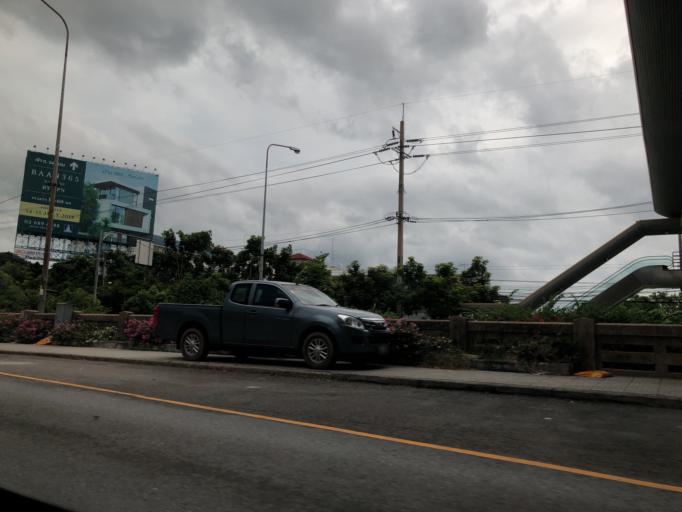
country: TH
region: Bangkok
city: Sathon
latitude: 13.7126
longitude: 100.5350
